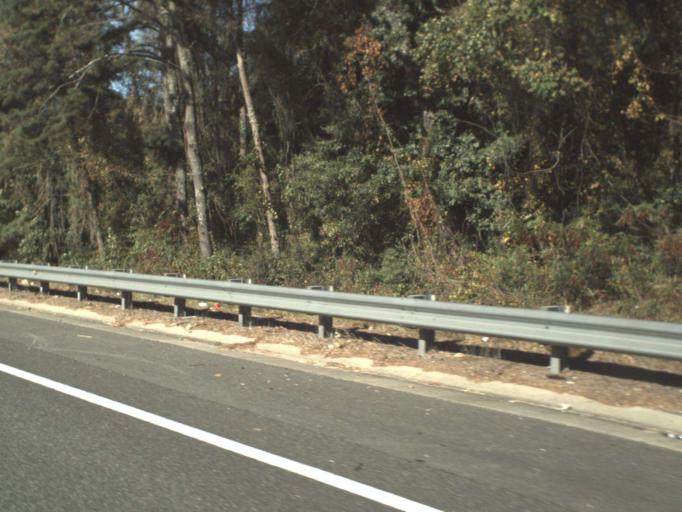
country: US
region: Florida
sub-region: Leon County
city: Tallahassee
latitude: 30.4983
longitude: -84.2661
